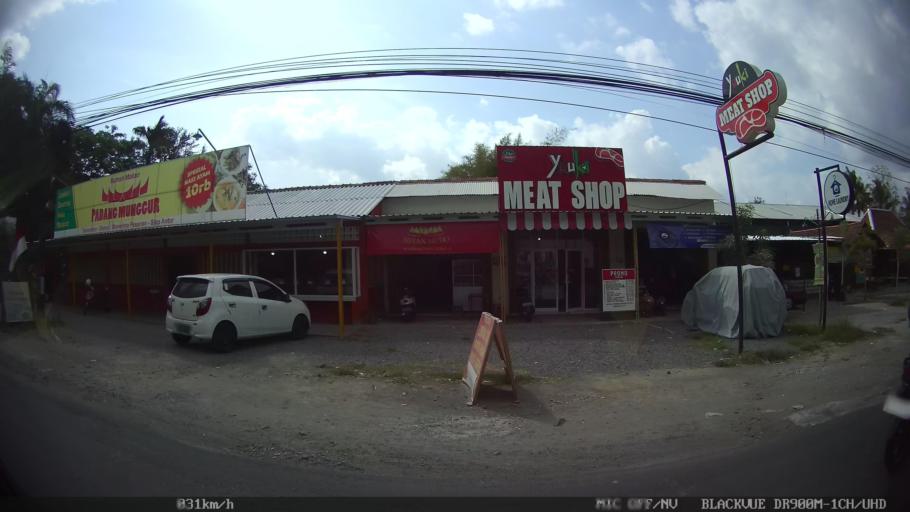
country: ID
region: Daerah Istimewa Yogyakarta
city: Kasihan
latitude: -7.8301
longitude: 110.3181
